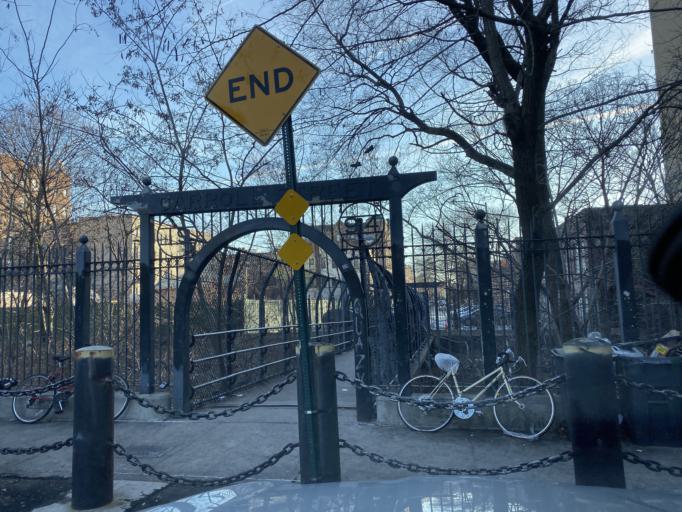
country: US
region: New York
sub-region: Kings County
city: Brooklyn
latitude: 40.6683
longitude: -73.9603
